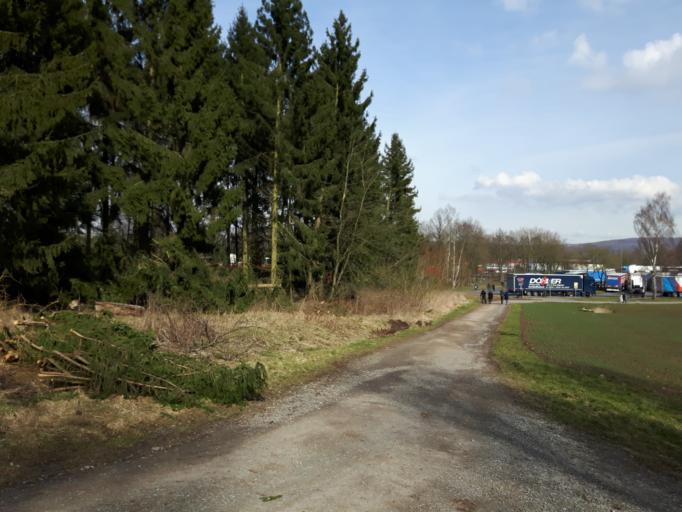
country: DE
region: Hesse
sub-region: Regierungsbezirk Kassel
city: Bad Arolsen
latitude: 51.4978
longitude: 8.9833
